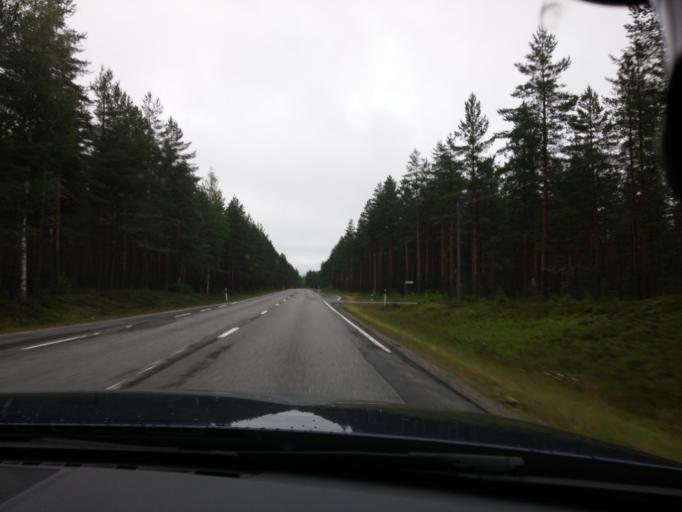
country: FI
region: Pirkanmaa
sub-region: Ylae-Pirkanmaa
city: Vilppula
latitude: 61.9420
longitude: 24.5415
